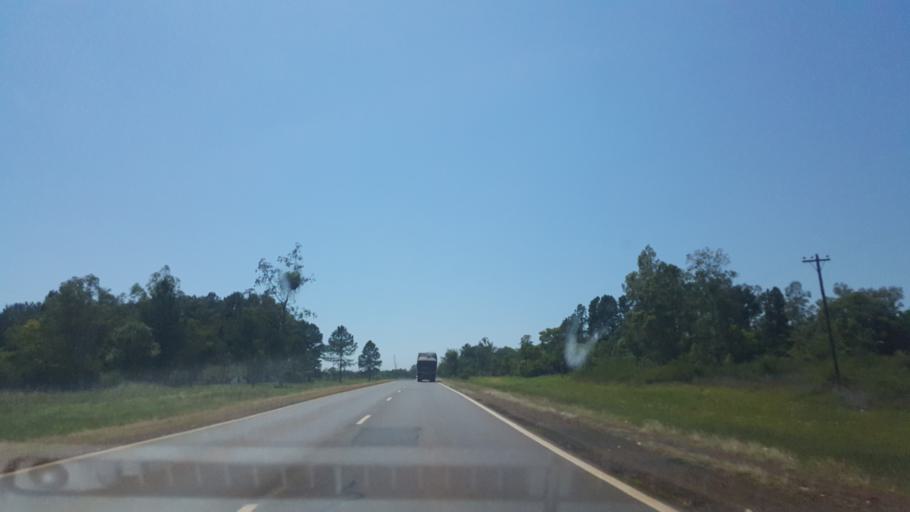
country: AR
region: Corrientes
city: Santo Tome
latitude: -28.5432
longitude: -56.0922
